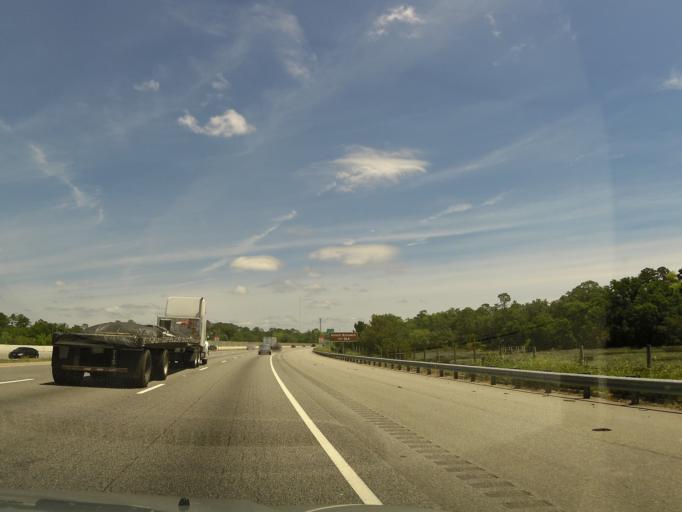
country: US
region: Georgia
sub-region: Glynn County
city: Dock Junction
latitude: 31.2119
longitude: -81.5321
